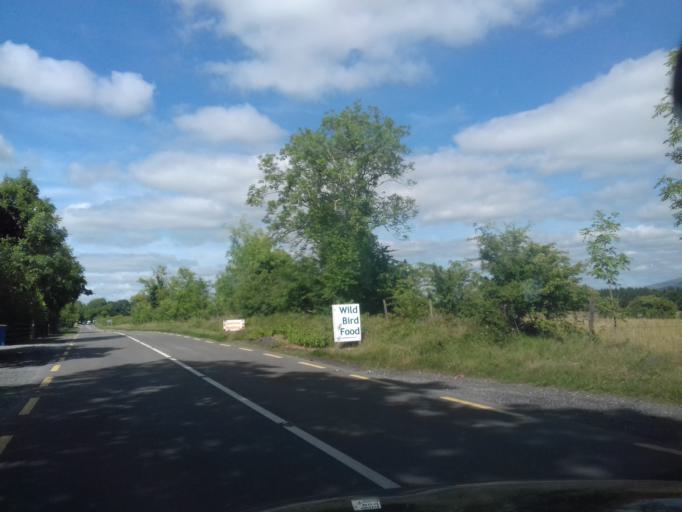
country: IE
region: Leinster
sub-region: Wicklow
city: Blessington
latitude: 53.1449
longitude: -6.5585
